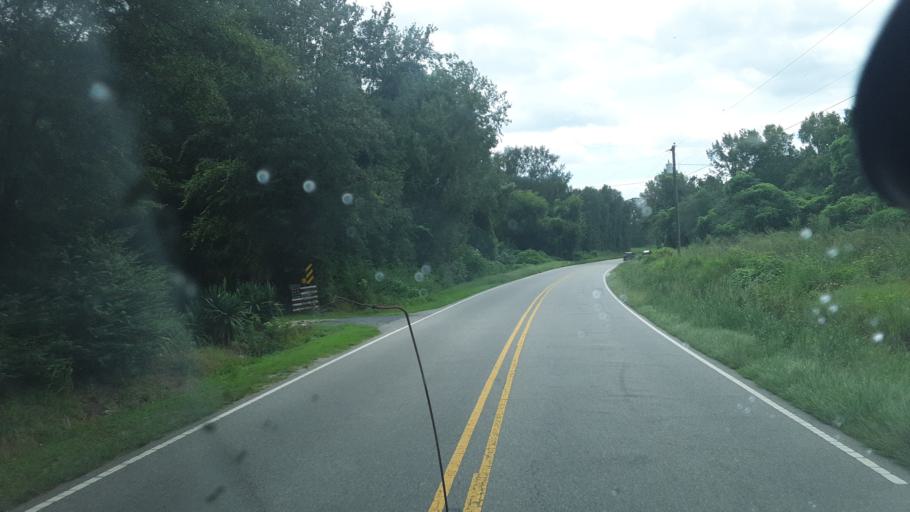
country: US
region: North Carolina
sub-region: Scotland County
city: Laurinburg
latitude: 34.6955
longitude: -79.4398
